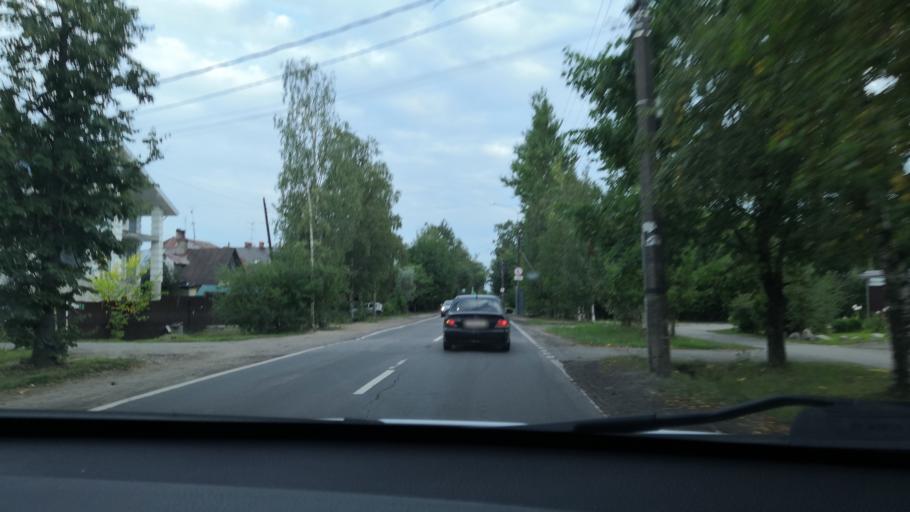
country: RU
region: St.-Petersburg
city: Pushkin
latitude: 59.7013
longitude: 30.4084
